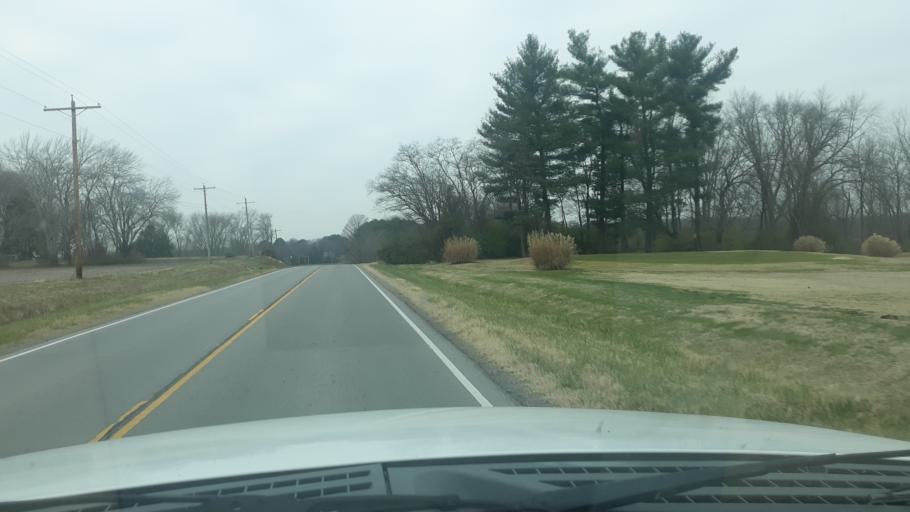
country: US
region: Illinois
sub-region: Saline County
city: Eldorado
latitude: 37.8216
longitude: -88.4904
